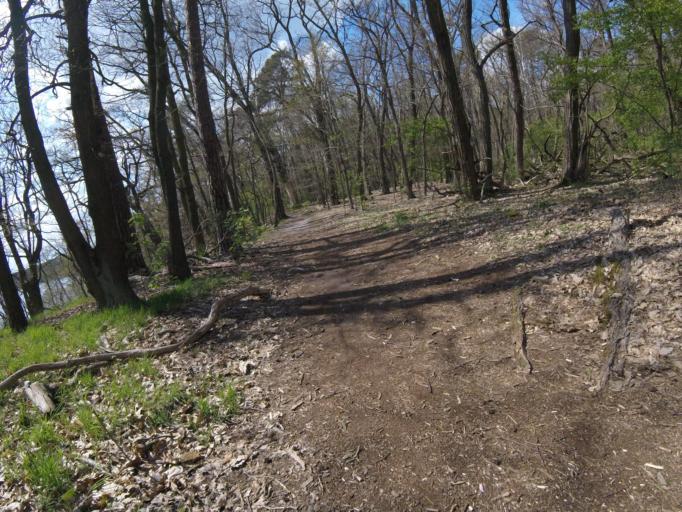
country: DE
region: Brandenburg
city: Gross Koris
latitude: 52.2002
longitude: 13.7196
